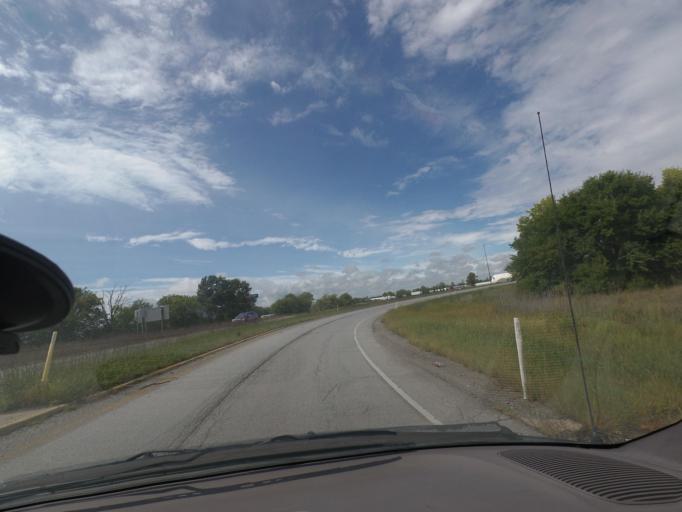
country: US
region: Indiana
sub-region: Montgomery County
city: Crawfordsville
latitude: 40.0788
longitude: -86.9056
